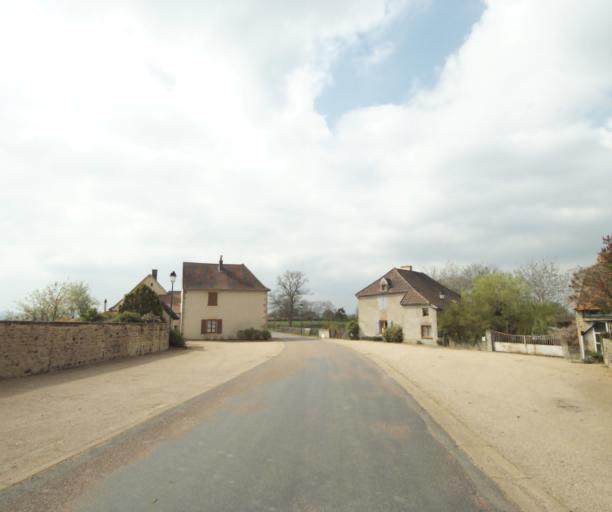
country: FR
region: Bourgogne
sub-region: Departement de Saone-et-Loire
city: Charolles
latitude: 46.3560
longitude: 4.2210
